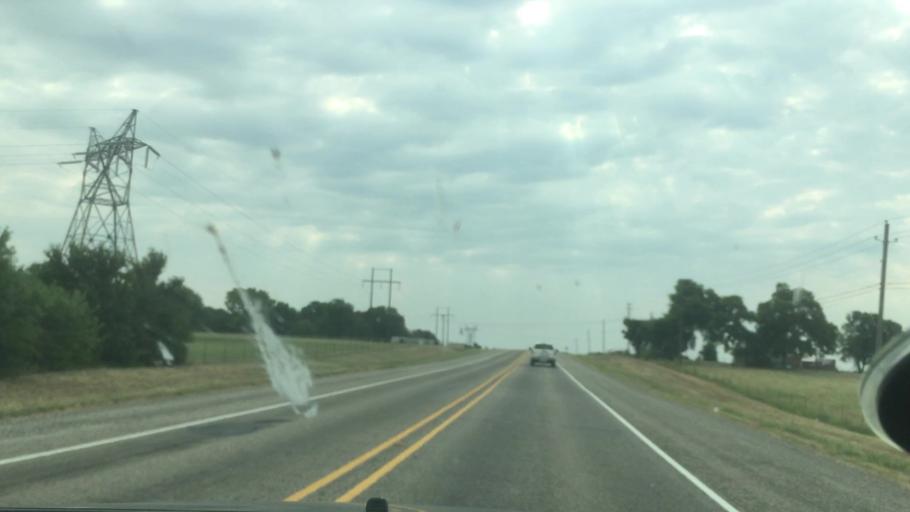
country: US
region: Texas
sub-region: Grayson County
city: Pottsboro
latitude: 33.7966
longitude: -96.6293
